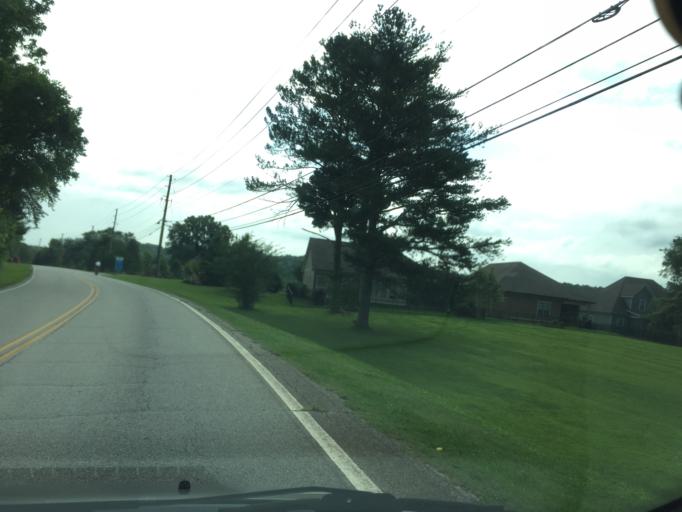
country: US
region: Tennessee
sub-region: Hamilton County
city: Apison
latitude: 35.0127
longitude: -85.0380
